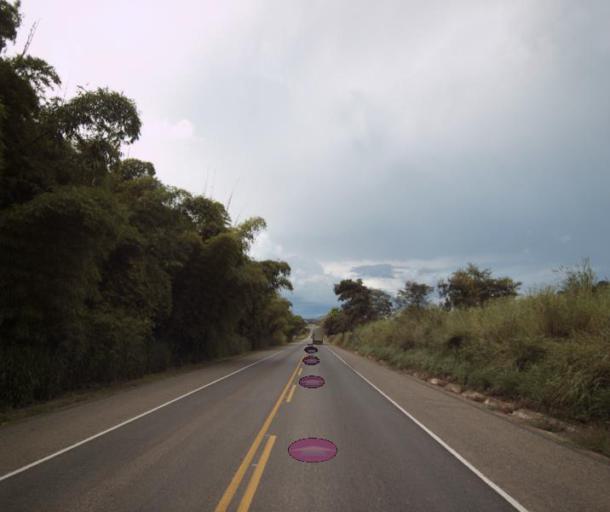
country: BR
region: Goias
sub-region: Ceres
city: Ceres
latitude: -15.2225
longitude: -49.5525
